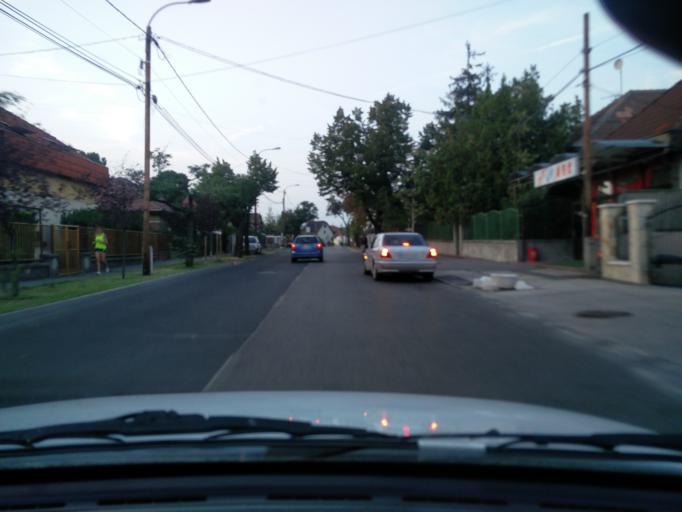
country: HU
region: Budapest
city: Budapest XXIII. keruelet
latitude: 47.4067
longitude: 19.0906
